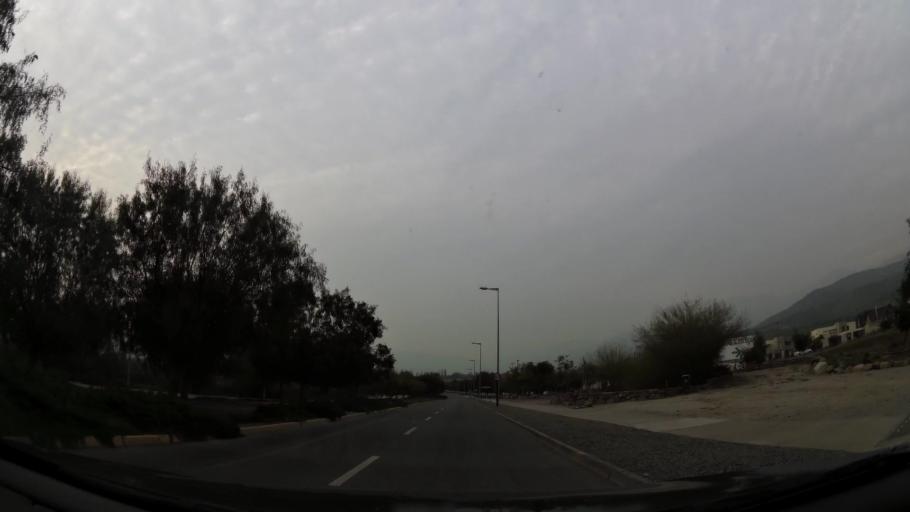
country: CL
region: Santiago Metropolitan
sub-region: Provincia de Chacabuco
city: Chicureo Abajo
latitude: -33.2713
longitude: -70.6245
